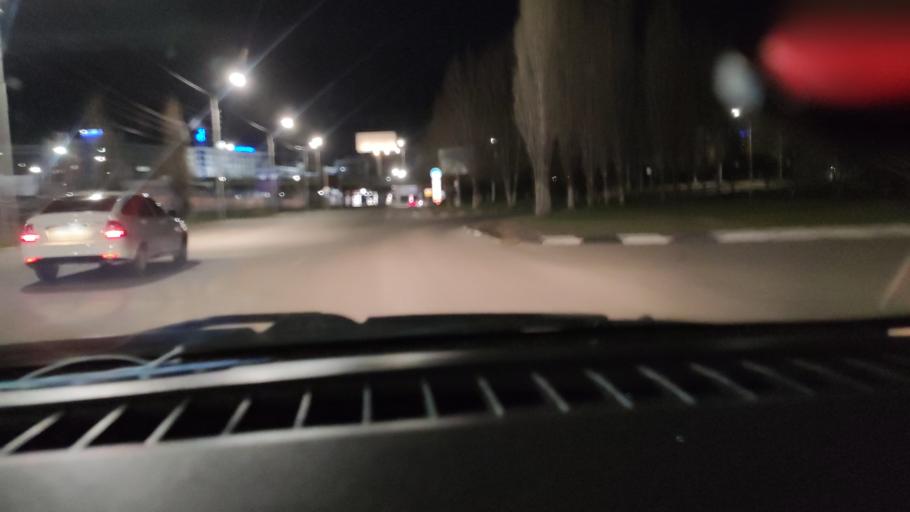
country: RU
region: Saratov
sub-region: Saratovskiy Rayon
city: Saratov
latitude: 51.5812
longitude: 45.9758
